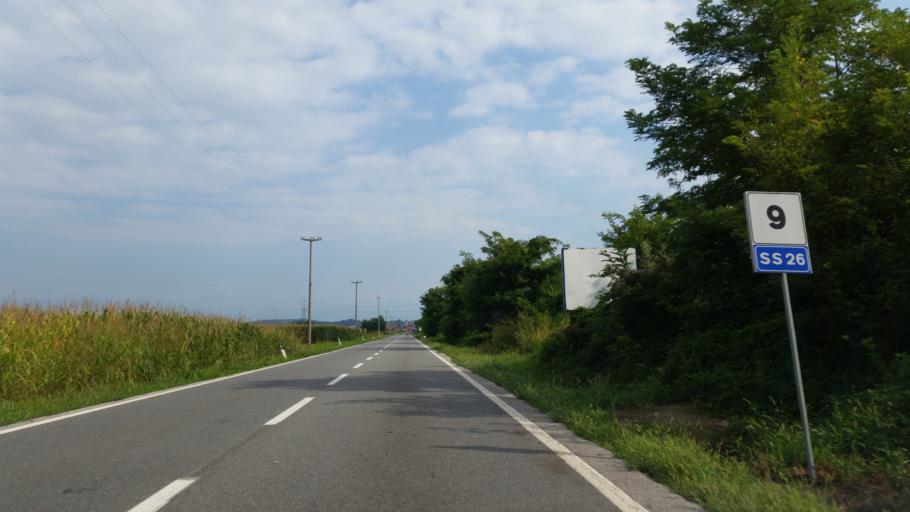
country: IT
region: Piedmont
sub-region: Provincia di Torino
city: Caluso
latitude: 45.2688
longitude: 7.8923
